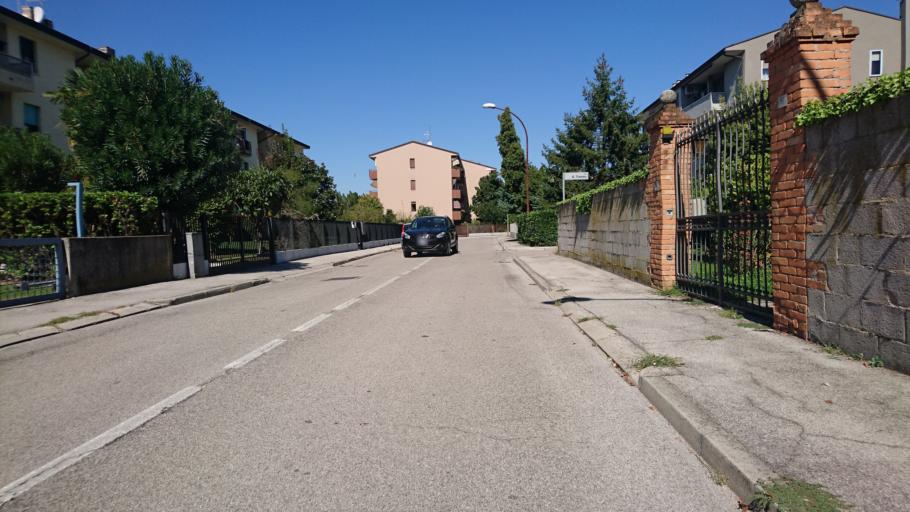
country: IT
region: Veneto
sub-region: Provincia di Venezia
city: Dolo
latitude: 45.4172
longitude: 12.0779
